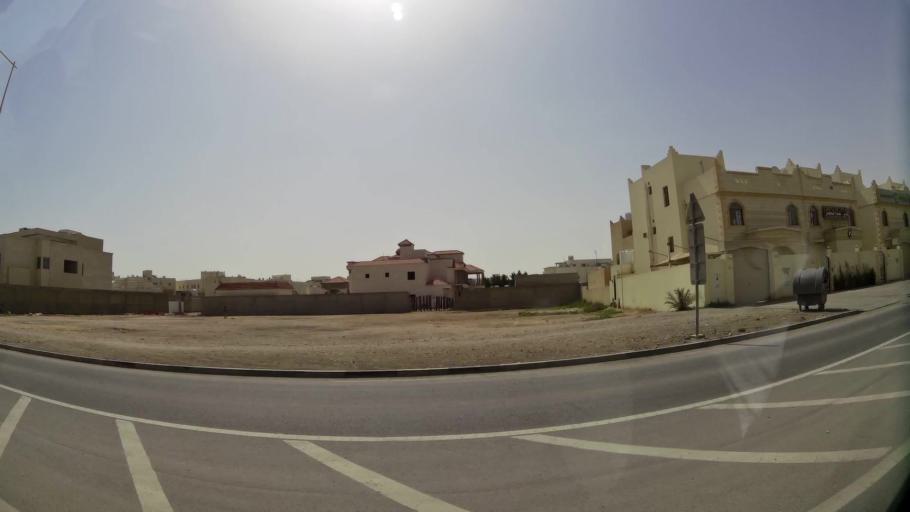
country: QA
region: Baladiyat Umm Salal
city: Umm Salal Muhammad
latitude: 25.3971
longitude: 51.4256
